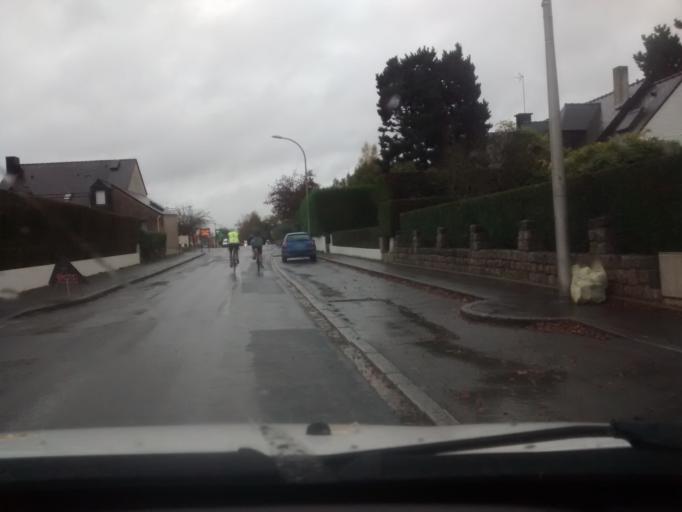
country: FR
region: Brittany
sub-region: Departement d'Ille-et-Vilaine
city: Fouillard
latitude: 48.1576
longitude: -1.5798
